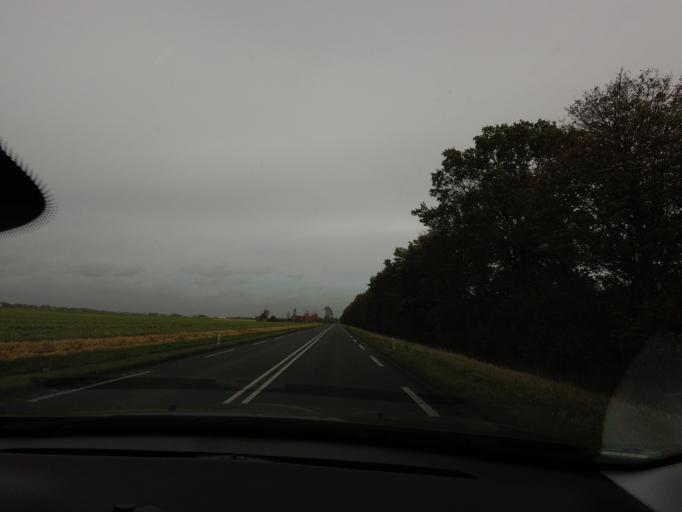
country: NL
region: Flevoland
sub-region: Gemeente Noordoostpolder
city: Ens
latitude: 52.7091
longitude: 5.8480
